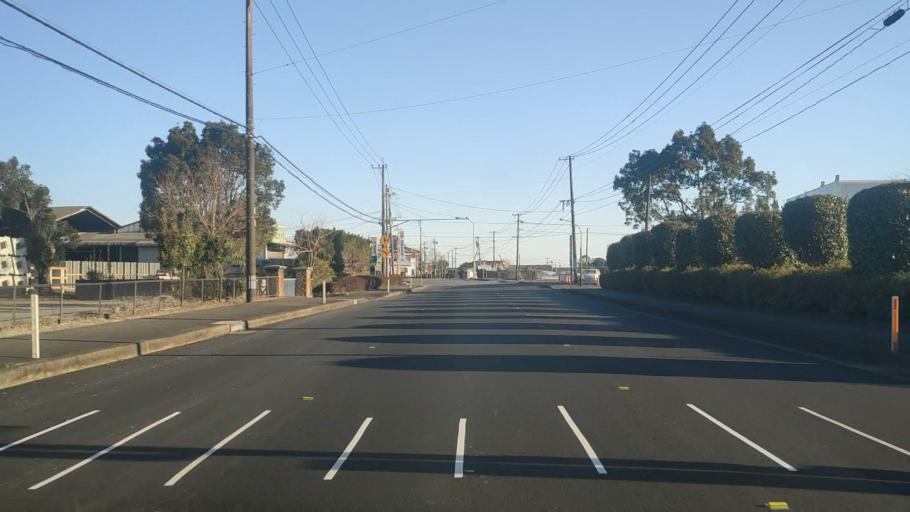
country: JP
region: Miyazaki
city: Takanabe
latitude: 32.2302
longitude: 131.5476
